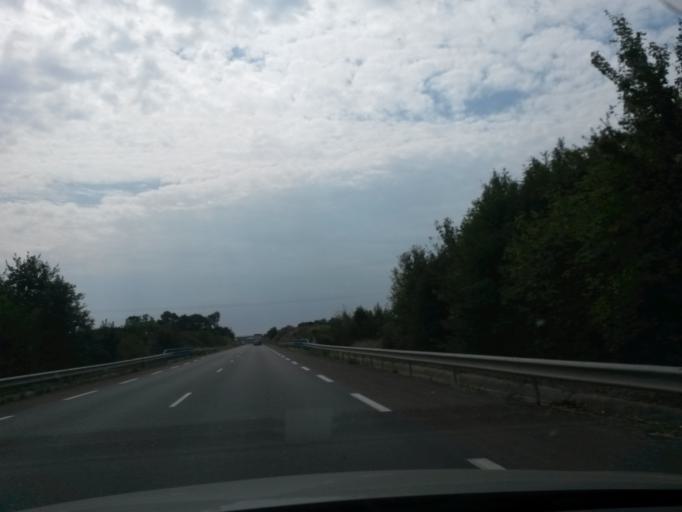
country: FR
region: Poitou-Charentes
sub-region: Departement de la Charente-Maritime
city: Saint-Xandre
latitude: 46.1894
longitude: -1.0941
